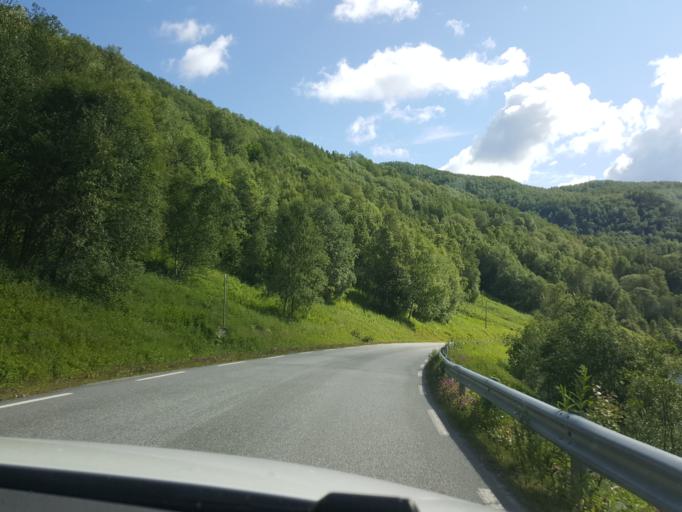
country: NO
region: Nordland
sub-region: Bodo
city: Loding
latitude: 67.0862
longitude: 14.9918
